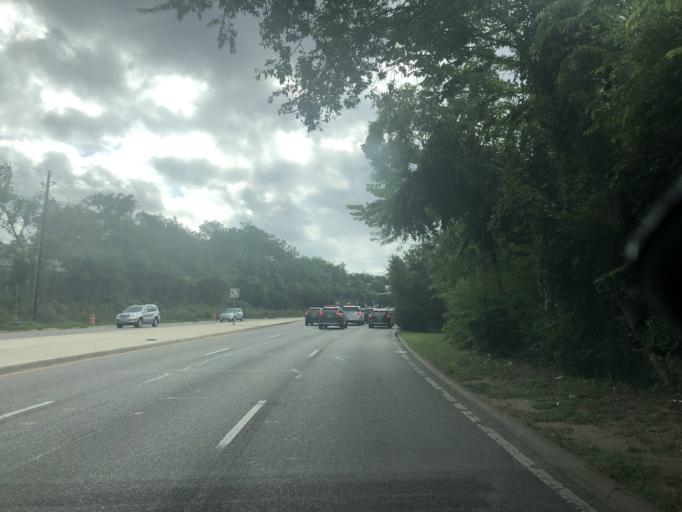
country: US
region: Texas
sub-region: Dallas County
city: University Park
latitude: 32.8668
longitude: -96.8242
